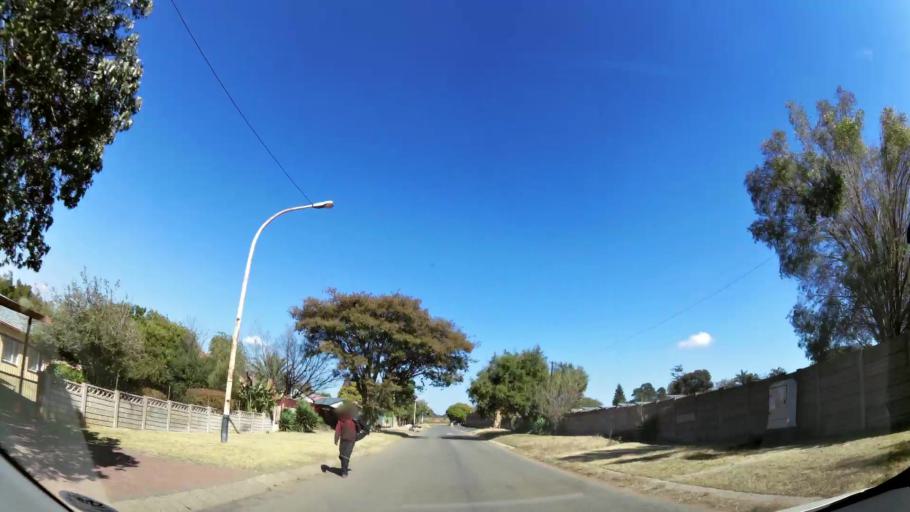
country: ZA
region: Mpumalanga
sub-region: Nkangala District Municipality
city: Witbank
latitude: -25.8484
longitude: 29.2426
